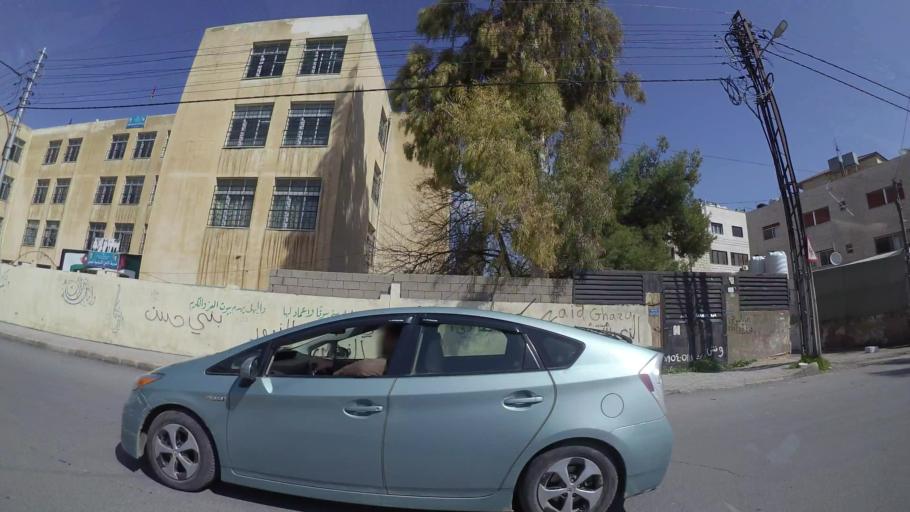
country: JO
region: Amman
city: Al Jubayhah
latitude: 31.9917
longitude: 35.9033
